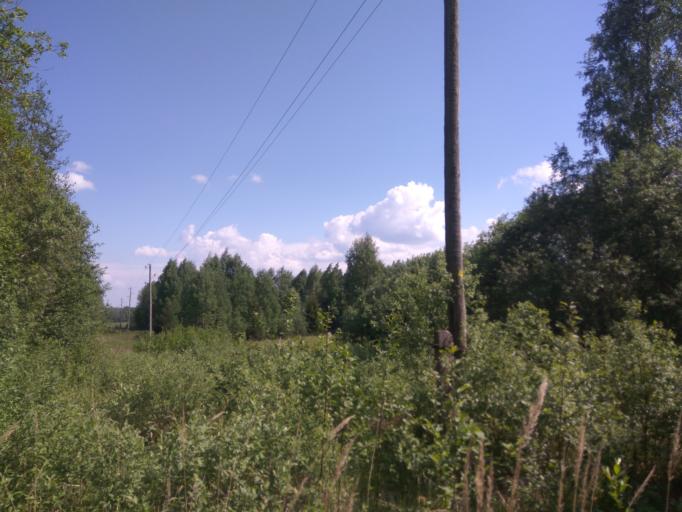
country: LV
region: Kuldigas Rajons
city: Kuldiga
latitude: 57.1753
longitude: 22.0160
